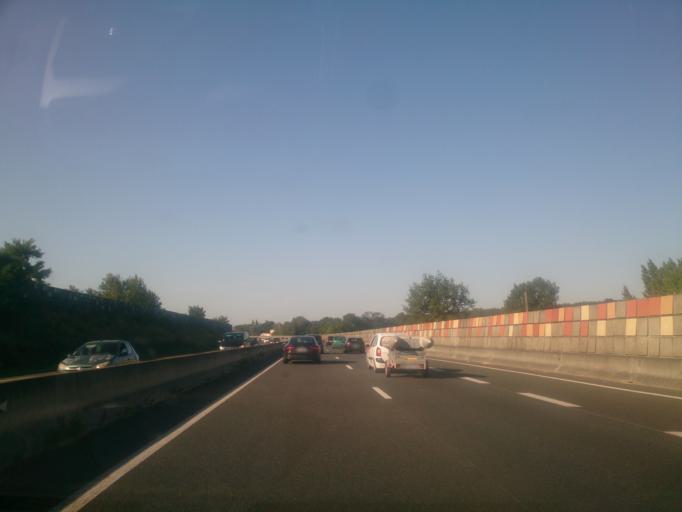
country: FR
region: Midi-Pyrenees
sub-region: Departement du Tarn-et-Garonne
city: Montauban
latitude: 44.0099
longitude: 1.3854
